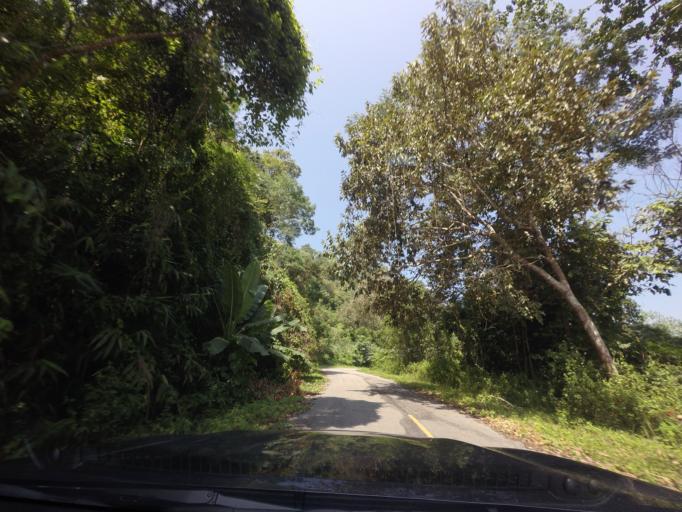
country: TH
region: Loei
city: Na Haeo
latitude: 17.5676
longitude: 100.9686
